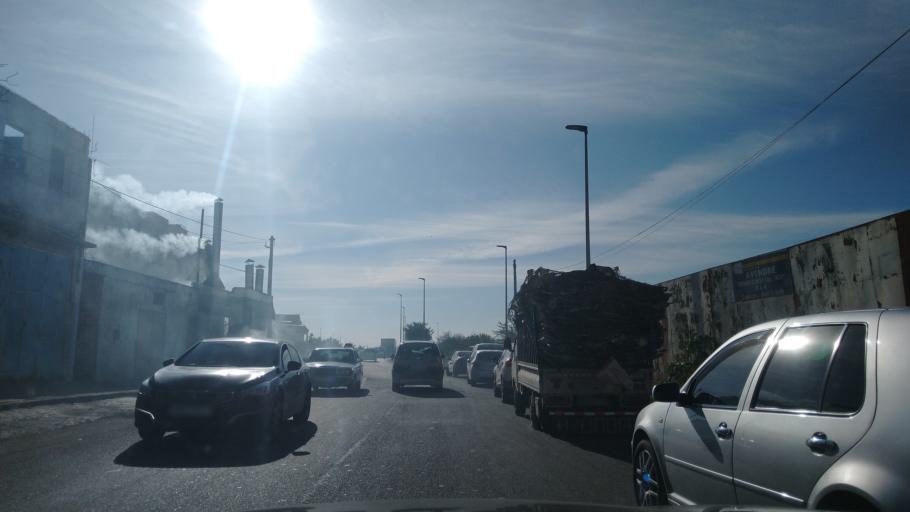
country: MA
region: Rabat-Sale-Zemmour-Zaer
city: Sale
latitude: 34.0034
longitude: -6.7471
